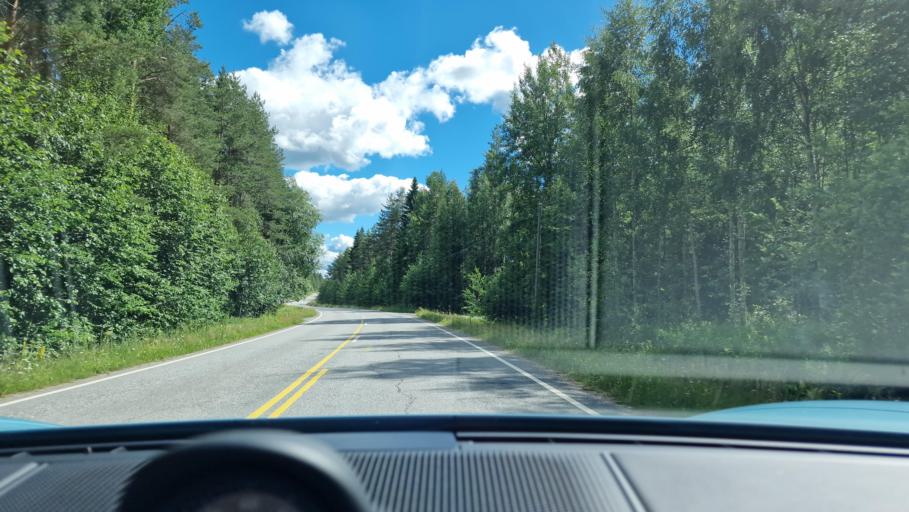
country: FI
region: Southern Ostrobothnia
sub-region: Jaerviseutu
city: Soini
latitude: 62.8244
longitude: 24.3430
